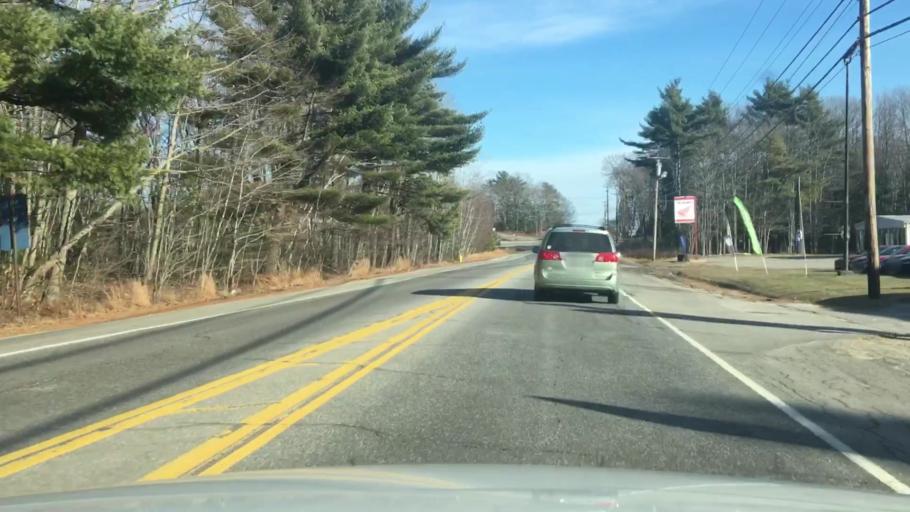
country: US
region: Maine
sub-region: Cumberland County
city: Brunswick
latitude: 43.9120
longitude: -69.8963
